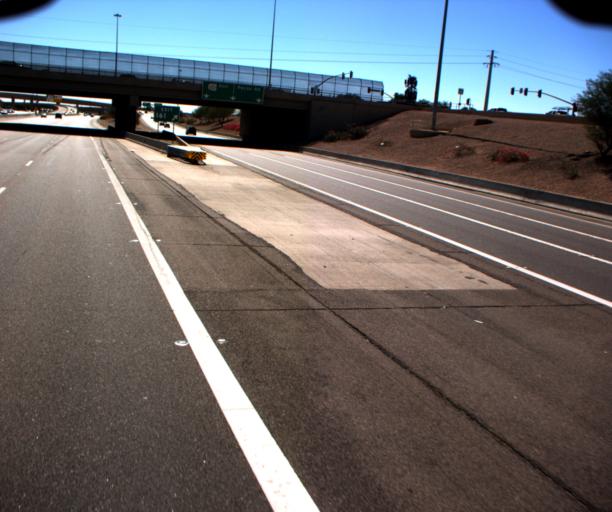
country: US
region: Arizona
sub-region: Maricopa County
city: Guadalupe
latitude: 33.3063
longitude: -111.9724
